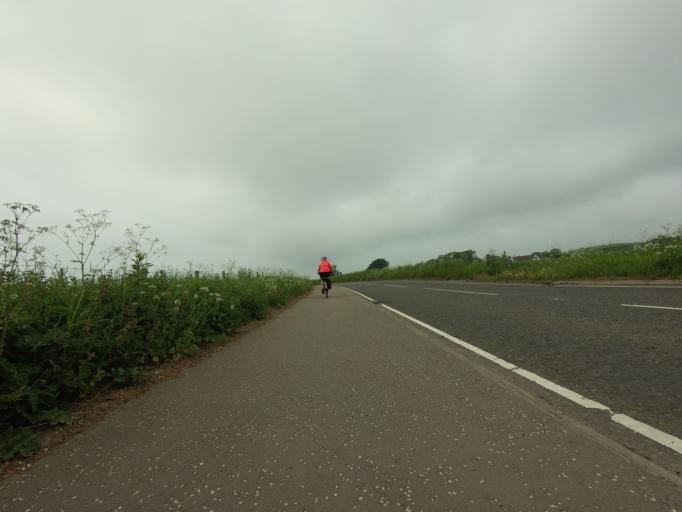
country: GB
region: Scotland
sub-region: Fife
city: Ballingry
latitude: 56.2229
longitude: -3.3526
